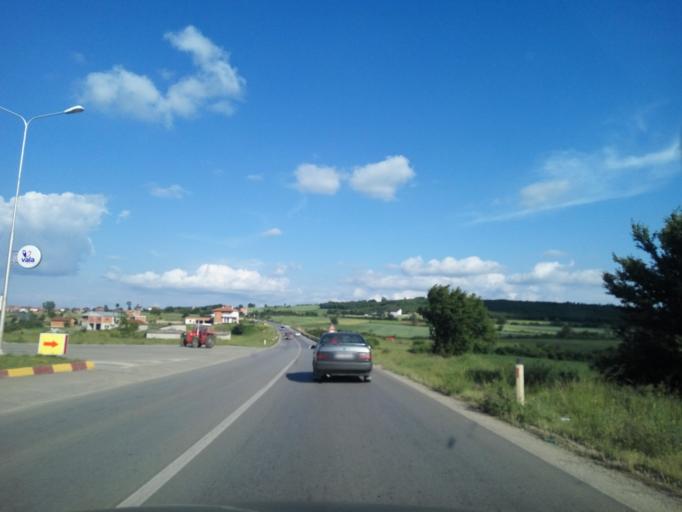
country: XK
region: Pec
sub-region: Komuna e Klines
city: Klina
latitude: 42.5895
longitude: 20.6673
